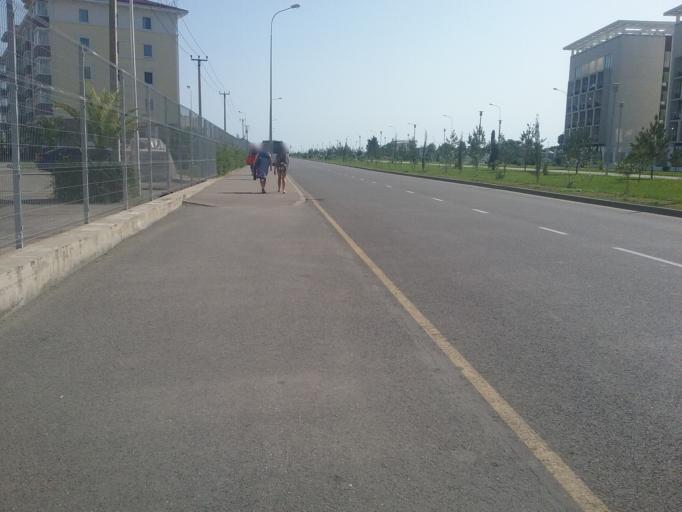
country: RU
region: Krasnodarskiy
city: Vysokoye
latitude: 43.3898
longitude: 39.9909
